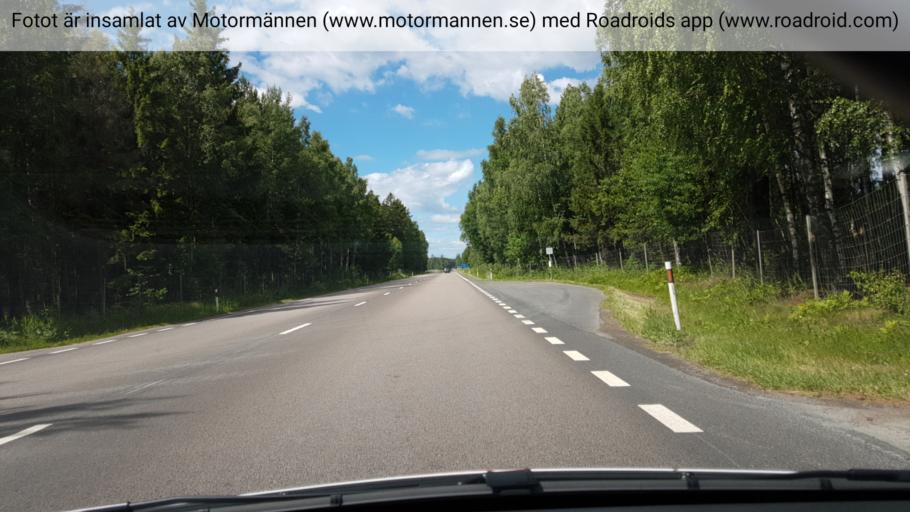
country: SE
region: Vaestra Goetaland
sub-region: Lidkopings Kommun
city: Vinninga
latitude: 58.4570
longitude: 13.2338
